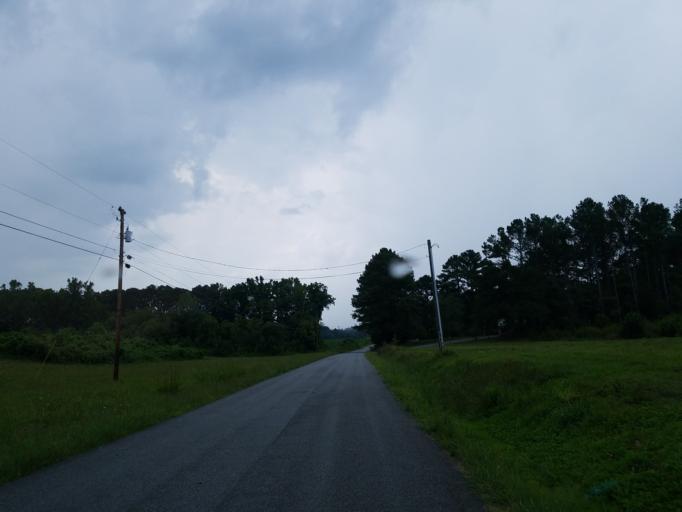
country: US
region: Georgia
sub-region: Bartow County
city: Rydal
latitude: 34.2678
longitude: -84.7589
